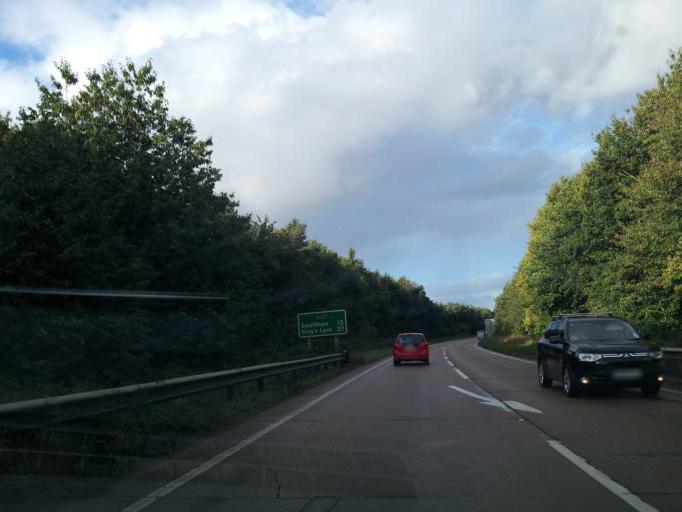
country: GB
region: England
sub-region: Norfolk
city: East Dereham
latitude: 52.6702
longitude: 0.9407
